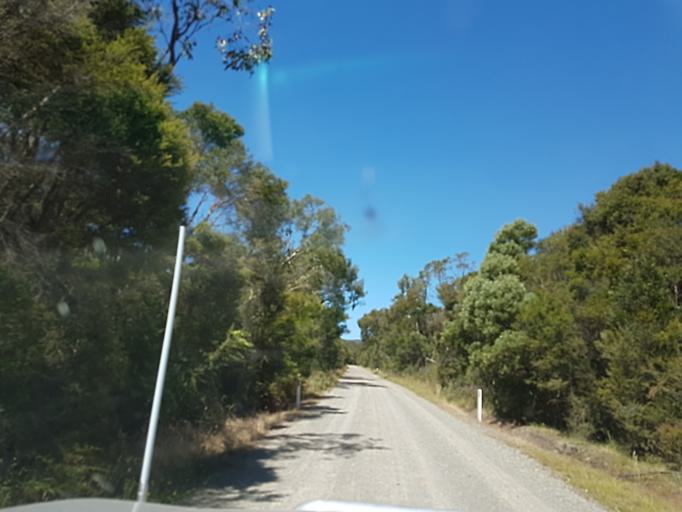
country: AU
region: Victoria
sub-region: Colac-Otway
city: Apollo Bay
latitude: -38.6632
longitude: 143.3416
